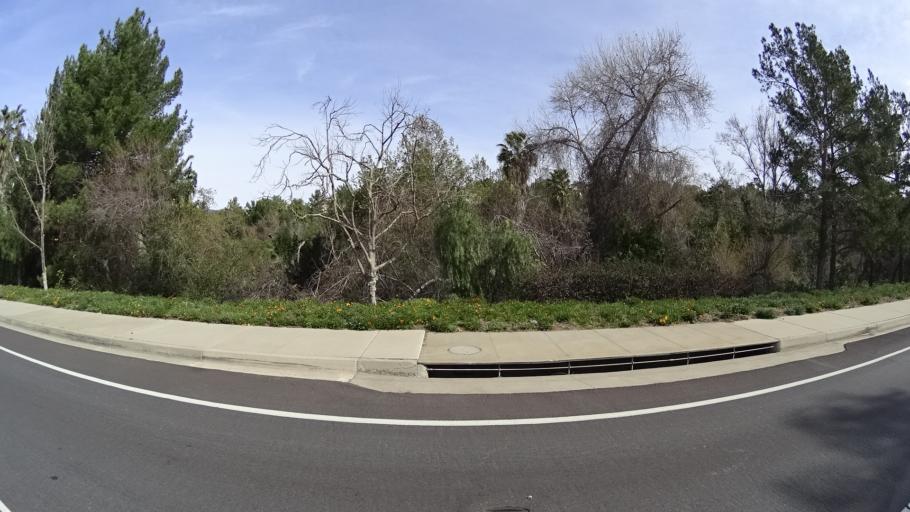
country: US
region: California
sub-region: Orange County
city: Yorba Linda
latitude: 33.8625
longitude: -117.7385
